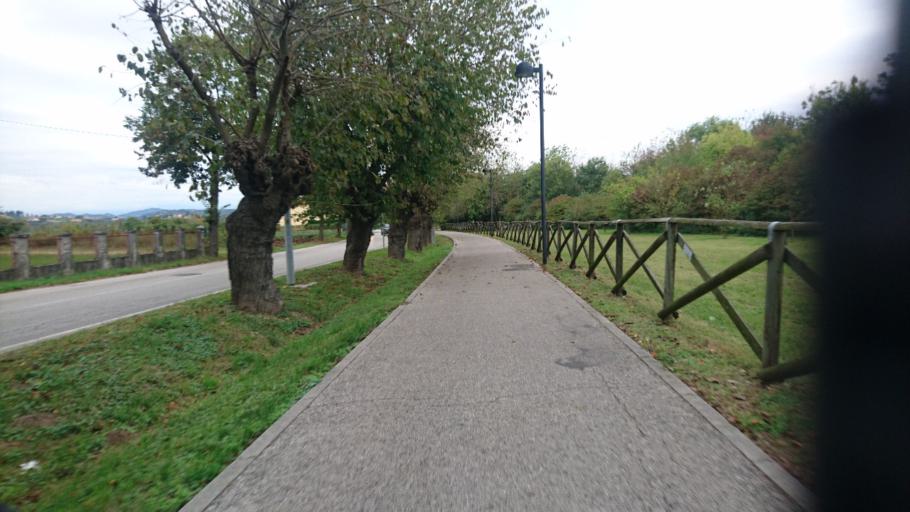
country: IT
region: Veneto
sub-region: Provincia di Vicenza
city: Montecchio Maggiore-Alte Ceccato
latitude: 45.5110
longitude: 11.4266
